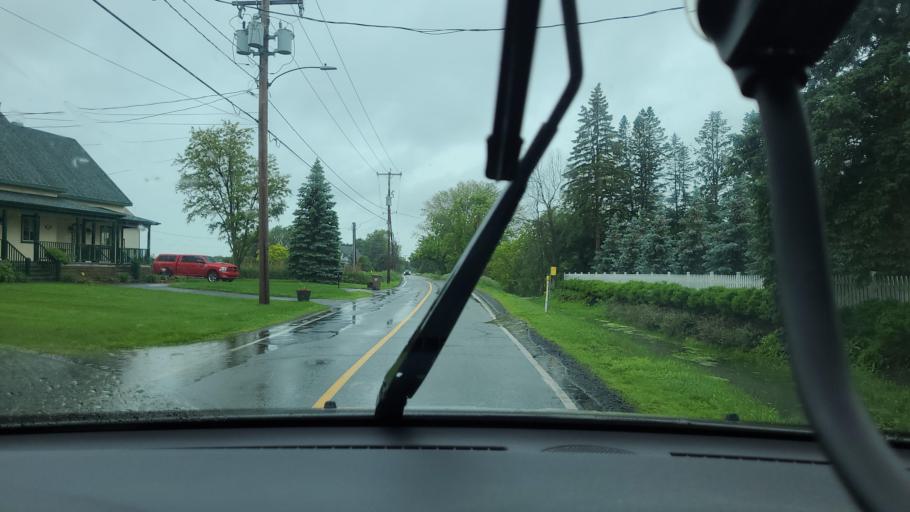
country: CA
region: Quebec
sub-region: Monteregie
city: Saint-Basile-le-Grand
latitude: 45.5543
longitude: -73.2676
